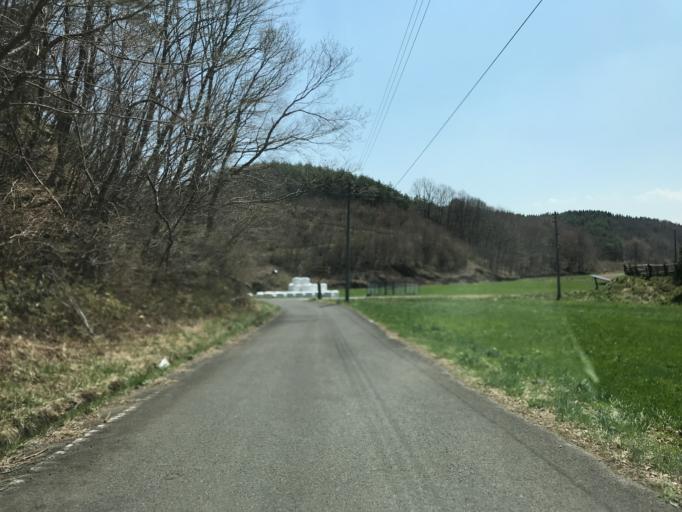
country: JP
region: Fukushima
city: Ishikawa
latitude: 36.9931
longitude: 140.5594
